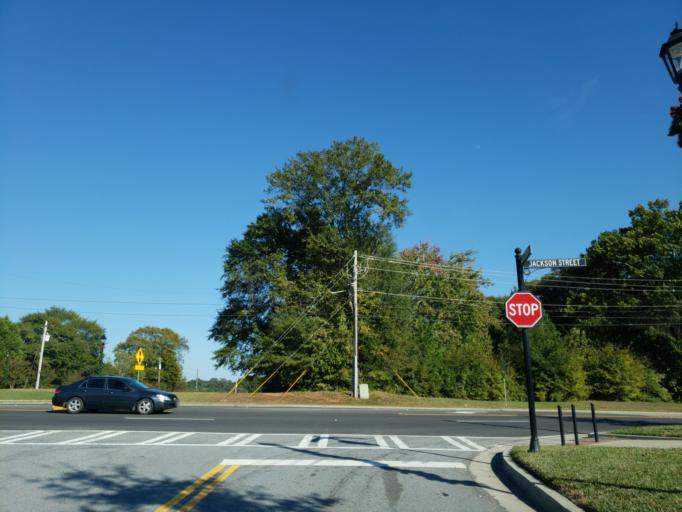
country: US
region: Georgia
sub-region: Gwinnett County
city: Lawrenceville
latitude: 33.9551
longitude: -83.9861
